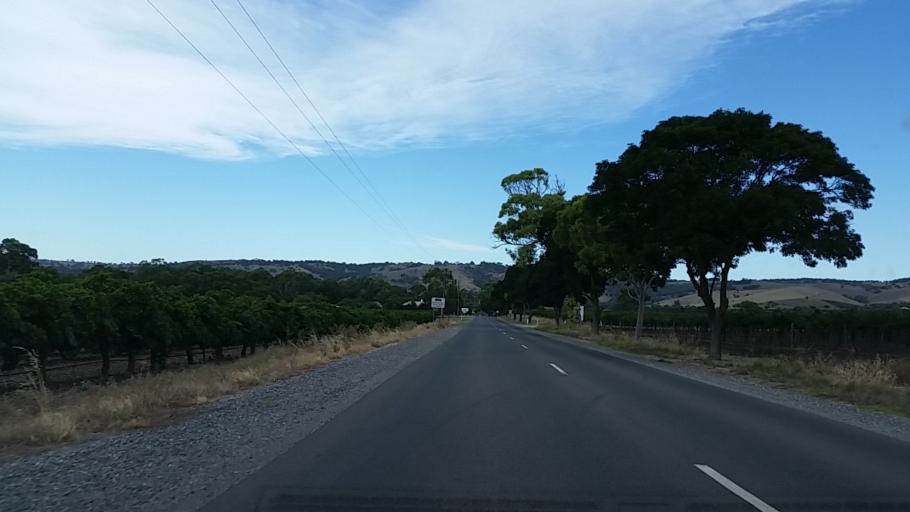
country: AU
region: South Australia
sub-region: Barossa
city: Tanunda
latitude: -34.5360
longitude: 138.9631
